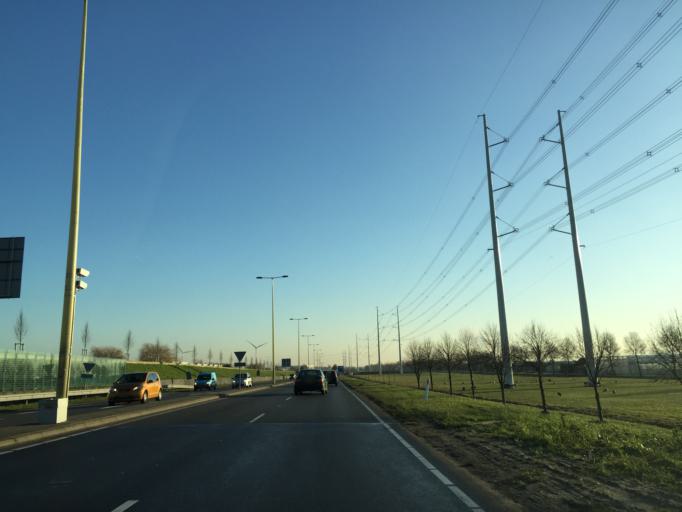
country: NL
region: South Holland
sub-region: Gemeente Zoetermeer
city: Zoetermeer
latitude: 52.0319
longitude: 4.4781
